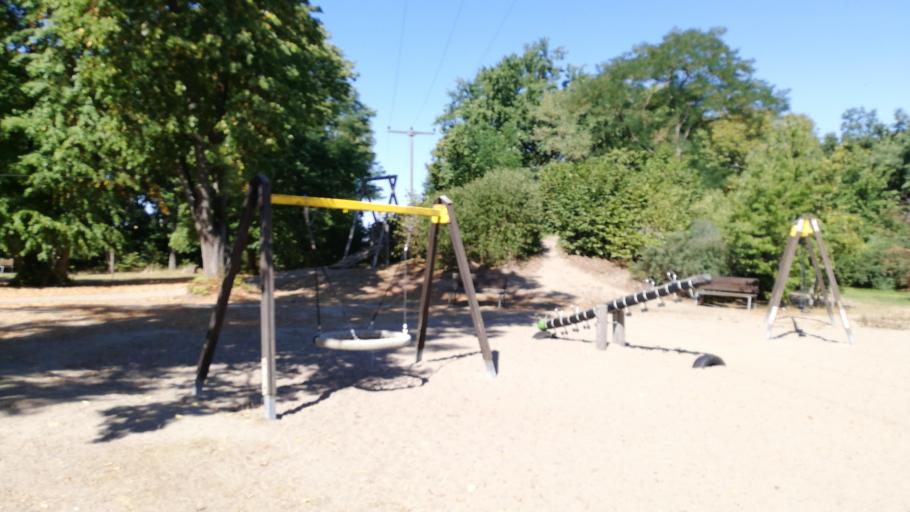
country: DE
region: Saxony-Anhalt
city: Genthin
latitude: 52.4589
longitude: 12.2118
